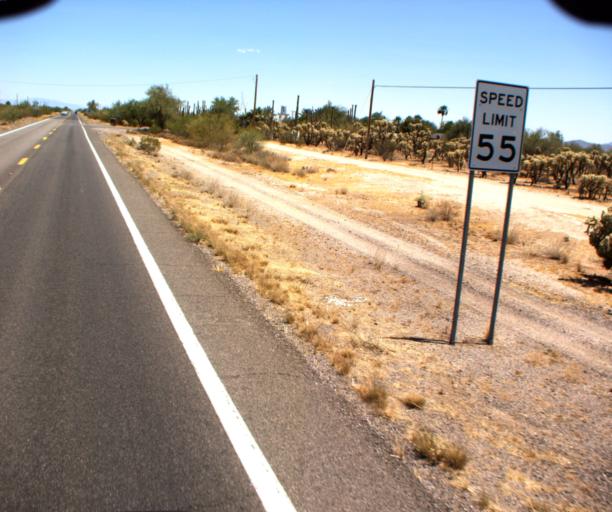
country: US
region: Arizona
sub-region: Pinal County
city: Florence
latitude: 32.9636
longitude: -111.3385
